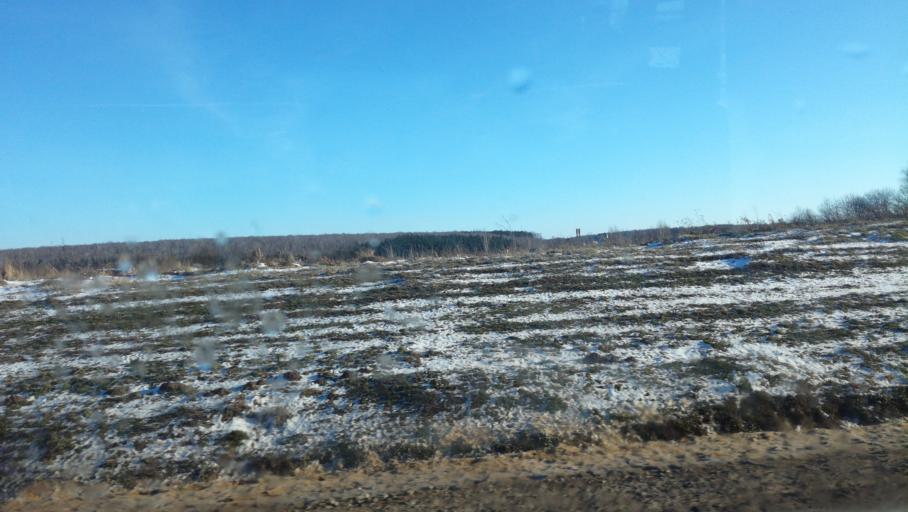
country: RU
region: Tula
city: Kosaya Gora
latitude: 54.1693
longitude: 37.4591
